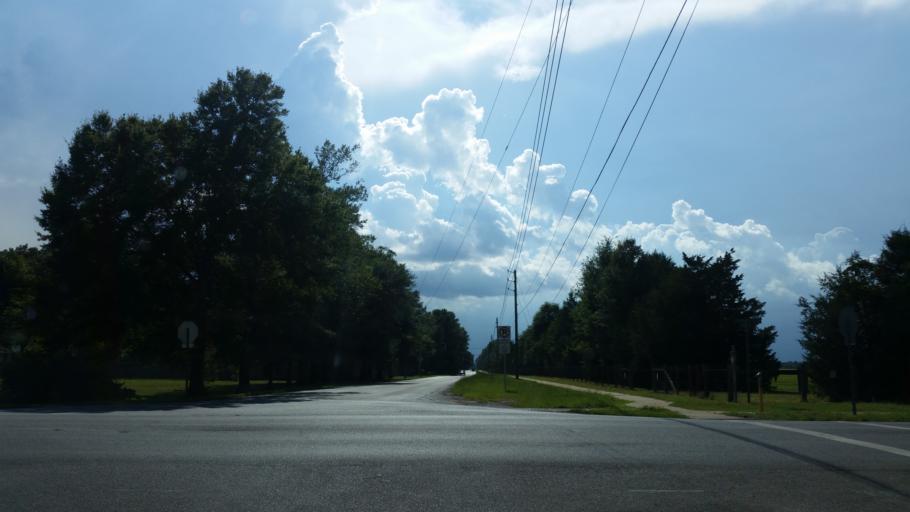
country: US
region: Florida
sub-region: Santa Rosa County
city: Pace
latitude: 30.6180
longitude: -87.1315
